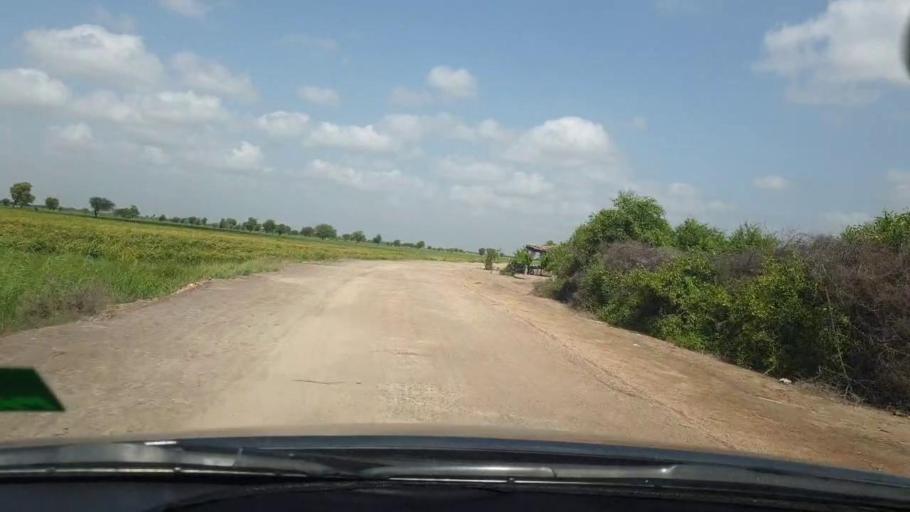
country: PK
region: Sindh
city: Tando Bago
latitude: 24.8569
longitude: 69.0588
